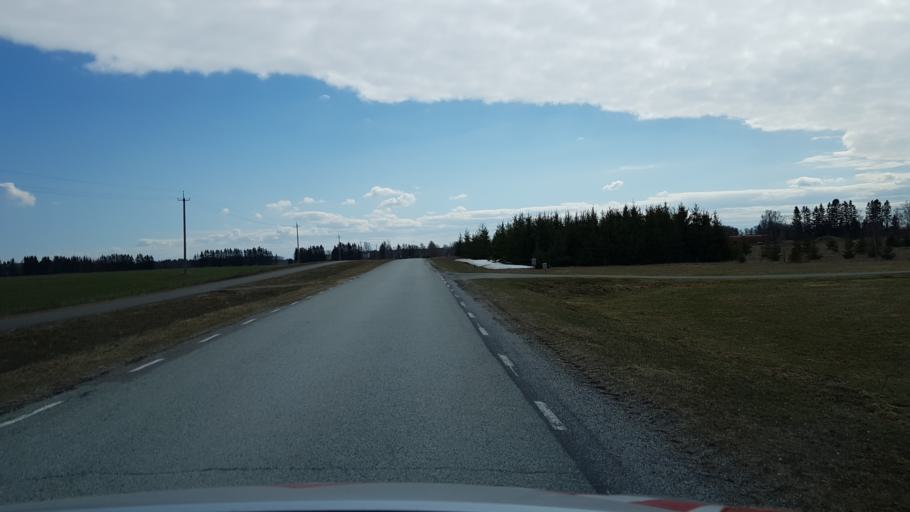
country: EE
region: Laeaene-Virumaa
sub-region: Haljala vald
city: Haljala
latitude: 59.4036
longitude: 26.2644
